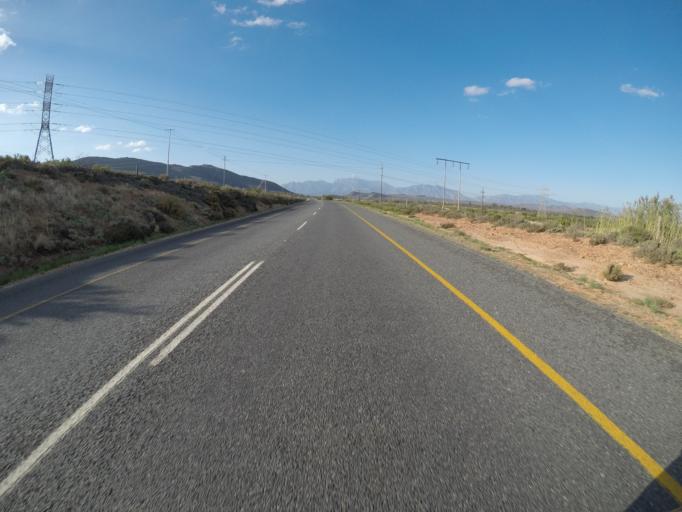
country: ZA
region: Western Cape
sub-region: Cape Winelands District Municipality
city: Worcester
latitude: -33.7705
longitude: 19.4728
